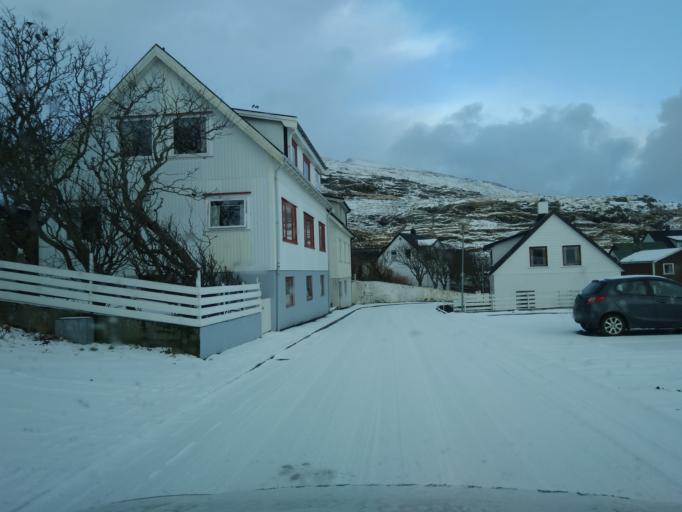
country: FO
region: Eysturoy
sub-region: Eidi
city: Eidi
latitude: 62.3008
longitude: -7.0924
